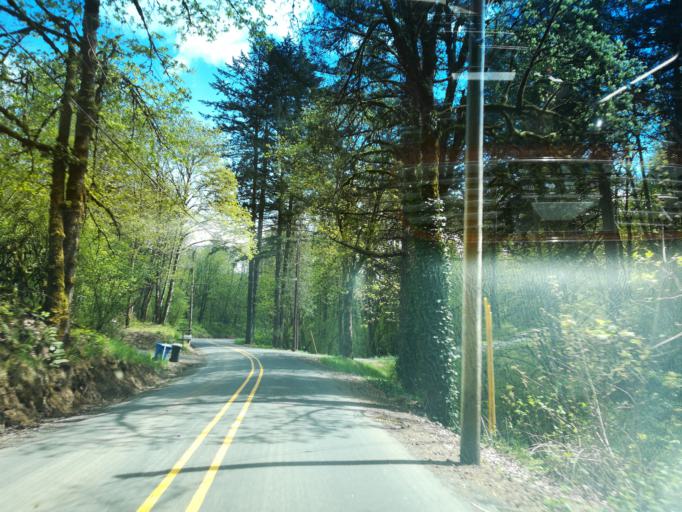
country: US
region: Oregon
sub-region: Clackamas County
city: Damascus
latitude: 45.4500
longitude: -122.4430
